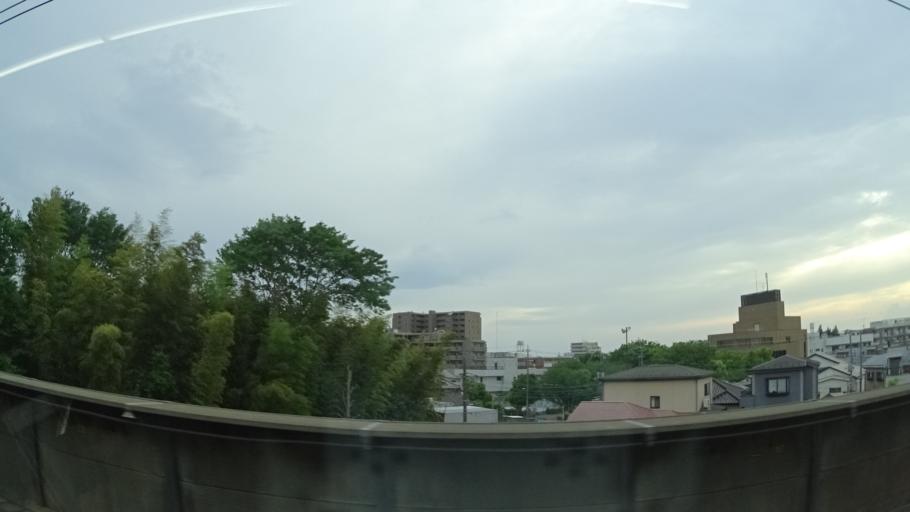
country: JP
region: Saitama
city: Shimotoda
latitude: 35.8132
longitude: 139.6721
